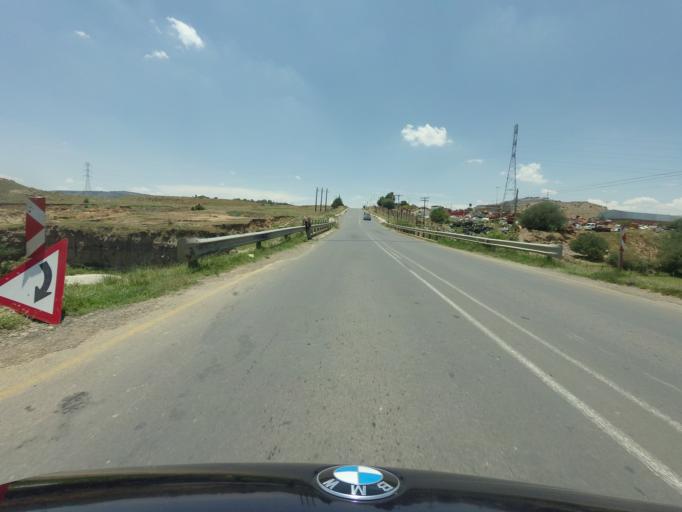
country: LS
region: Maseru
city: Maseru
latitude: -29.2650
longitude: 27.5501
